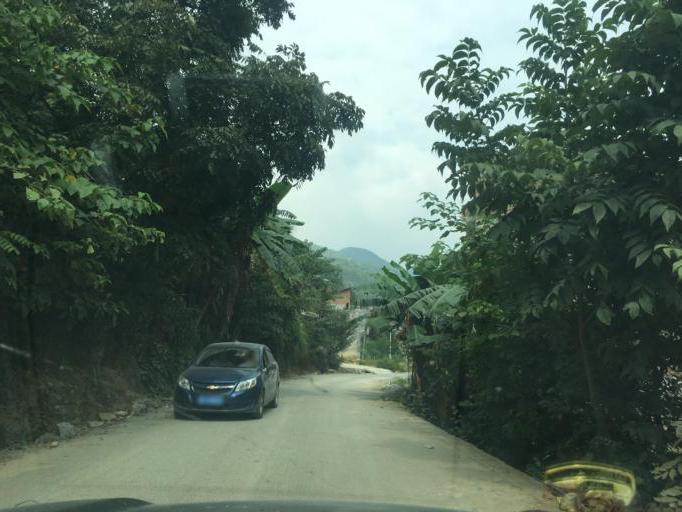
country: CN
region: Guangxi Zhuangzu Zizhiqu
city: Tongle
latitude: 25.3308
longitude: 105.9923
